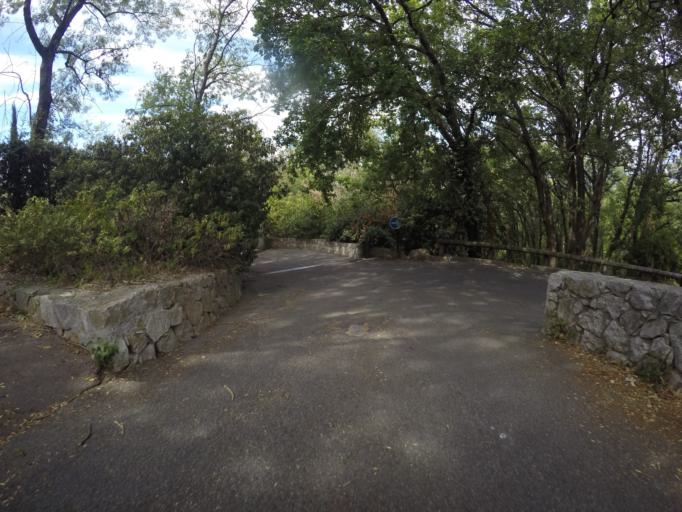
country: FR
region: Provence-Alpes-Cote d'Azur
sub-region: Departement des Alpes-Maritimes
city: Mougins
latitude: 43.6014
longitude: 6.9939
